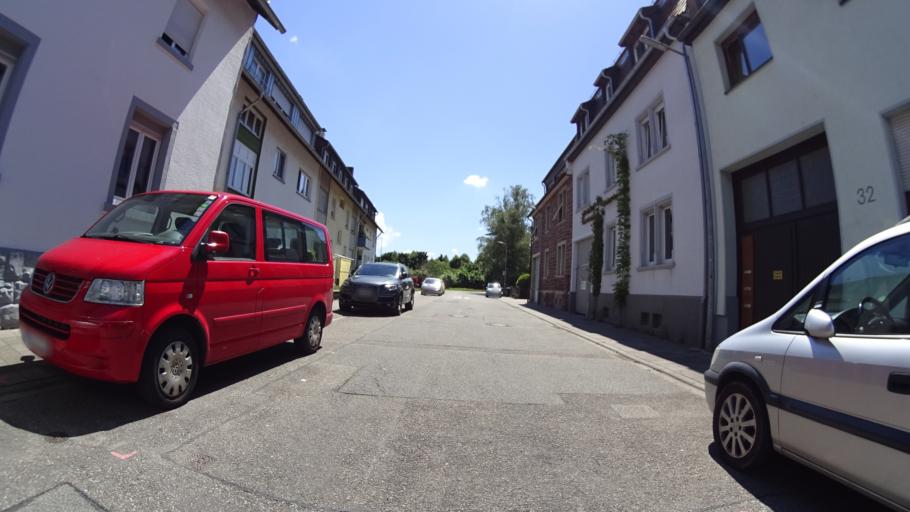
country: DE
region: Baden-Wuerttemberg
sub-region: Karlsruhe Region
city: Karlsruhe
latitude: 48.9889
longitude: 8.4535
